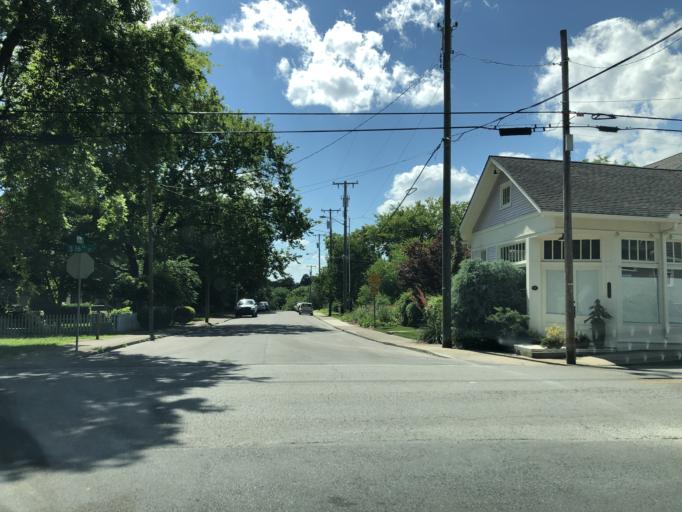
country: US
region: Tennessee
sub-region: Davidson County
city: Nashville
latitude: 36.1744
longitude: -86.7421
